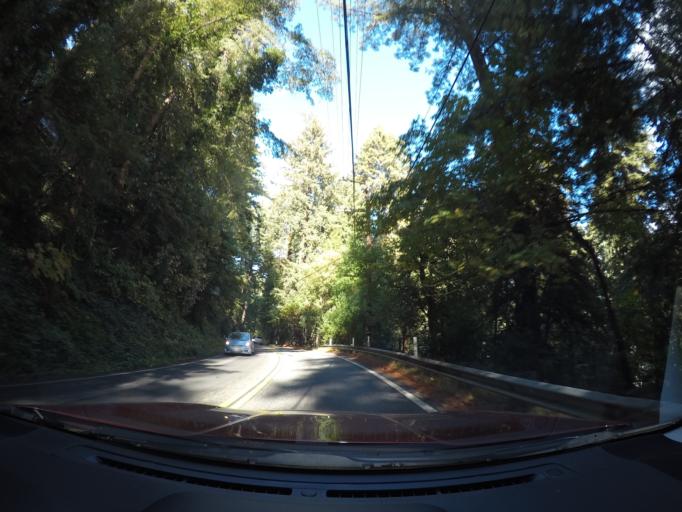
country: US
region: California
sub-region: Santa Cruz County
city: Ben Lomond
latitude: 37.0838
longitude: -122.0885
